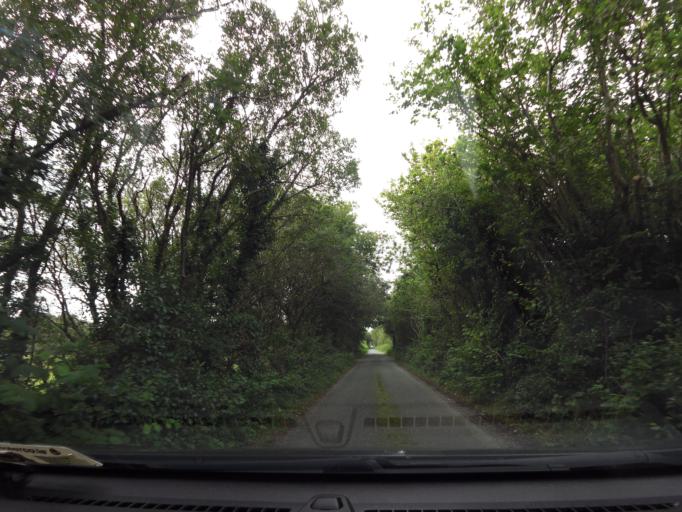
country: IE
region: Connaught
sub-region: County Galway
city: Moycullen
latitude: 53.3399
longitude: -9.1598
